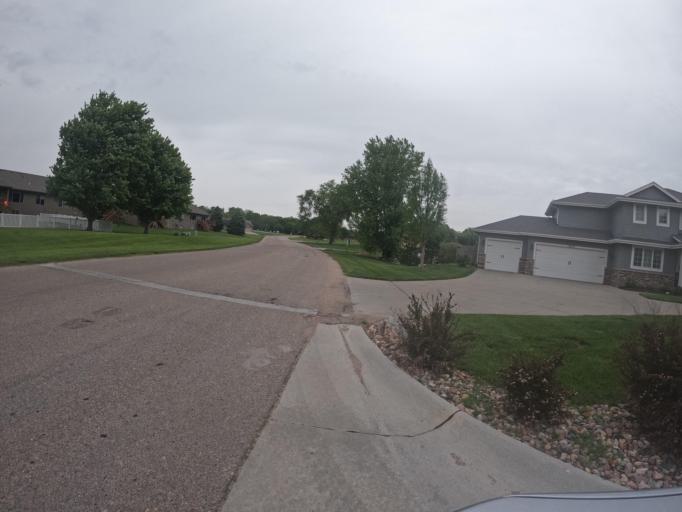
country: US
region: Nebraska
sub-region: Sarpy County
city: Offutt Air Force Base
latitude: 41.0499
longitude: -95.9577
